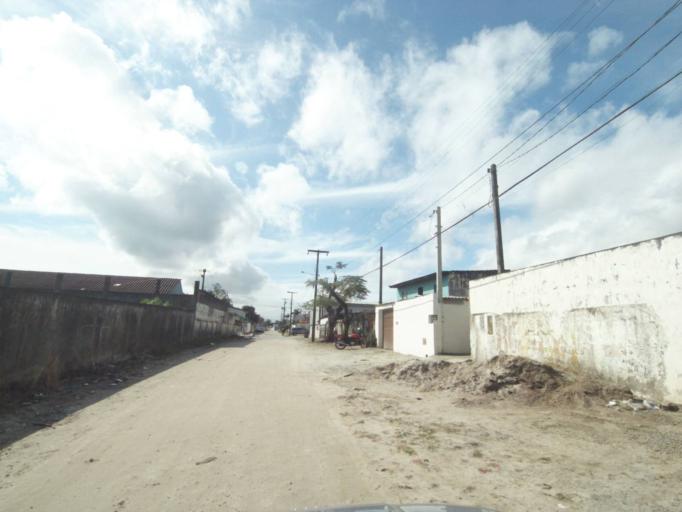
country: BR
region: Parana
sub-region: Paranagua
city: Paranagua
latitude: -25.5684
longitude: -48.5652
